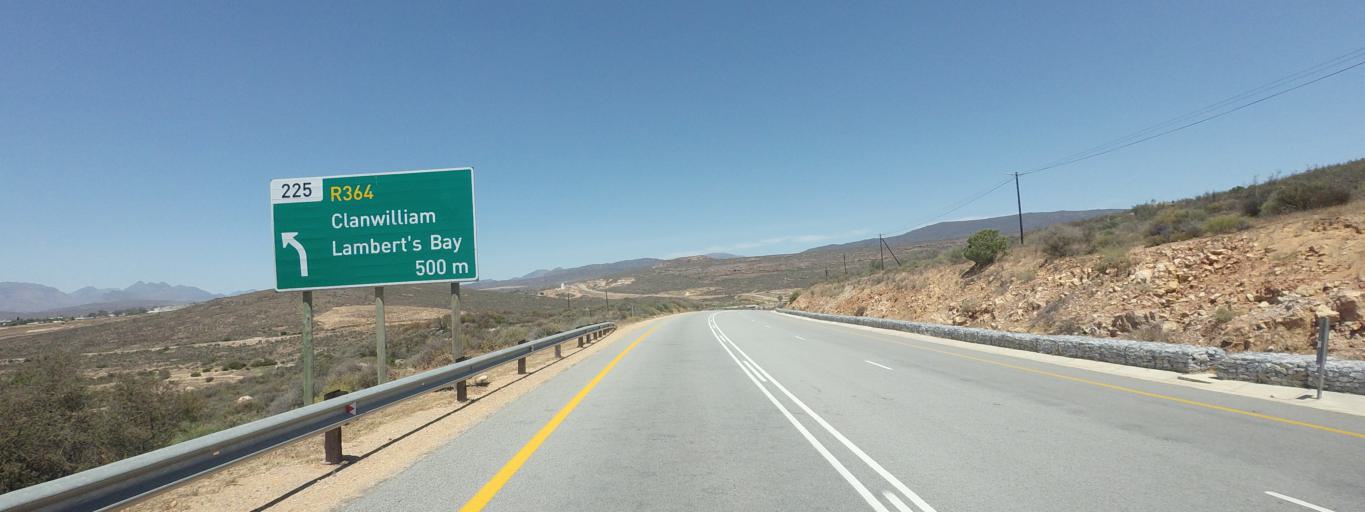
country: ZA
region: Western Cape
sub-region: West Coast District Municipality
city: Clanwilliam
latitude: -32.1653
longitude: 18.8719
